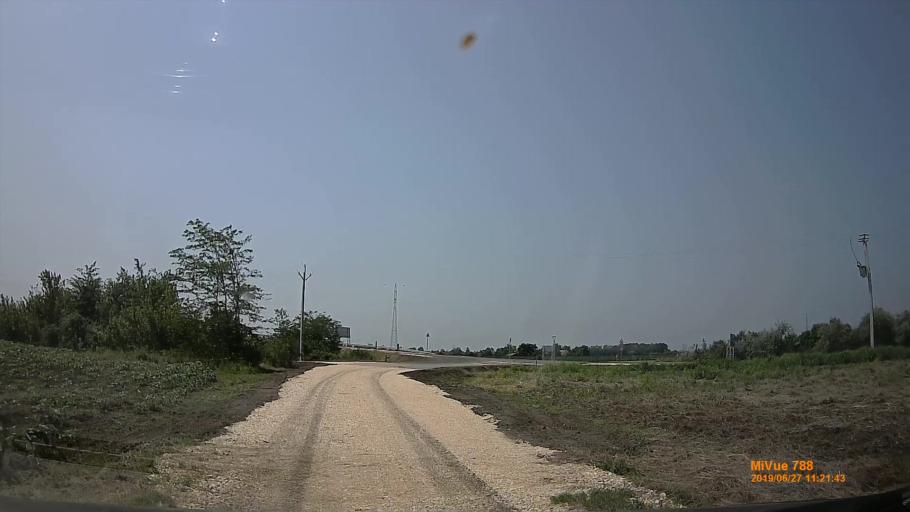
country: HU
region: Pest
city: Cegled
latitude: 47.2042
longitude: 19.7842
